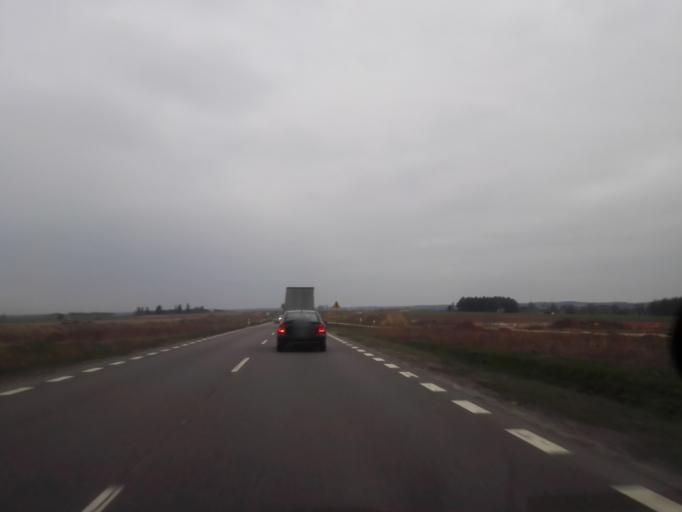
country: PL
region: Podlasie
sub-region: Powiat grajewski
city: Szczuczyn
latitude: 53.5807
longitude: 22.3199
